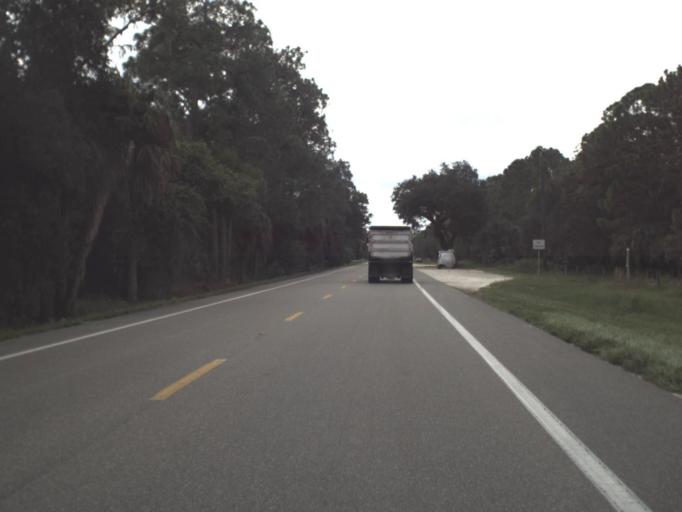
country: US
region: Florida
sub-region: Charlotte County
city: Cleveland
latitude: 26.9673
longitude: -81.7607
